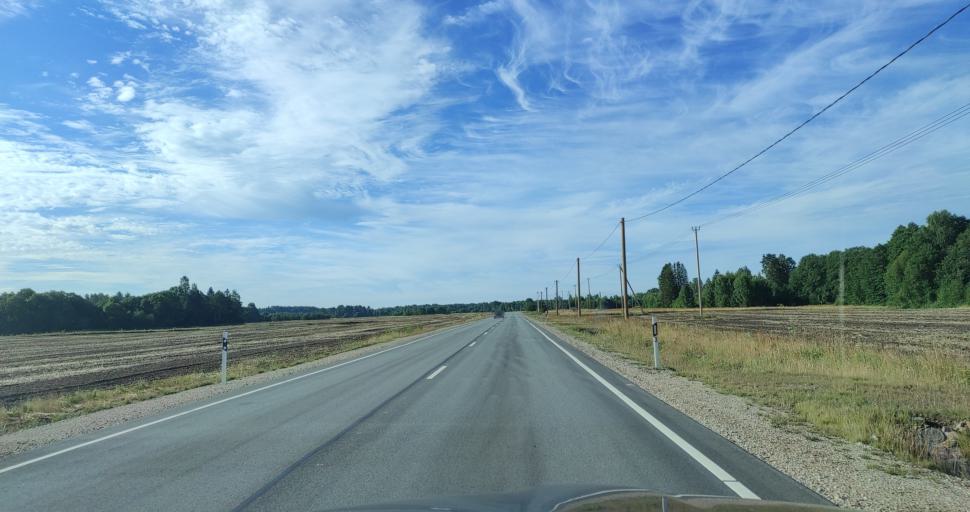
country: LV
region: Pavilostas
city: Pavilosta
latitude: 56.8236
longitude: 21.2266
